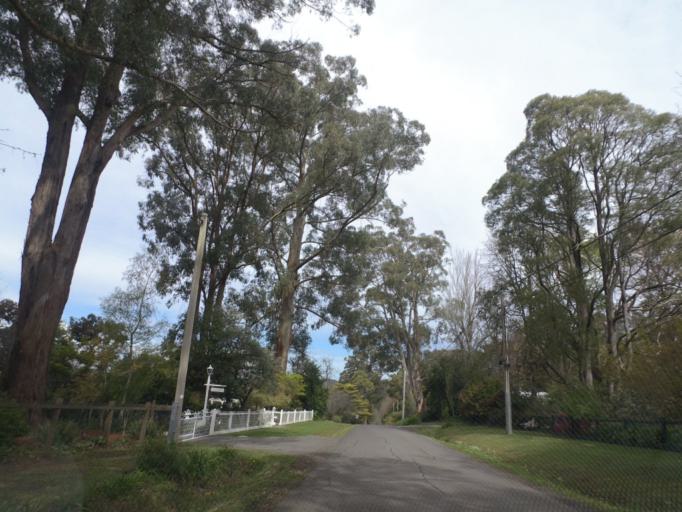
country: AU
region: Victoria
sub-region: Yarra Ranges
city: Mount Dandenong
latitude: -37.8300
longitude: 145.3662
